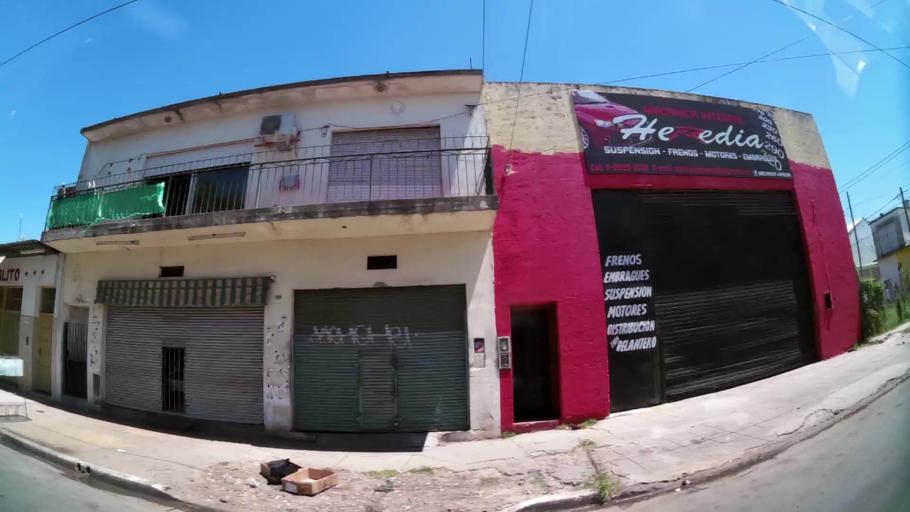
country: AR
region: Buenos Aires
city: Hurlingham
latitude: -34.5070
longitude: -58.6759
